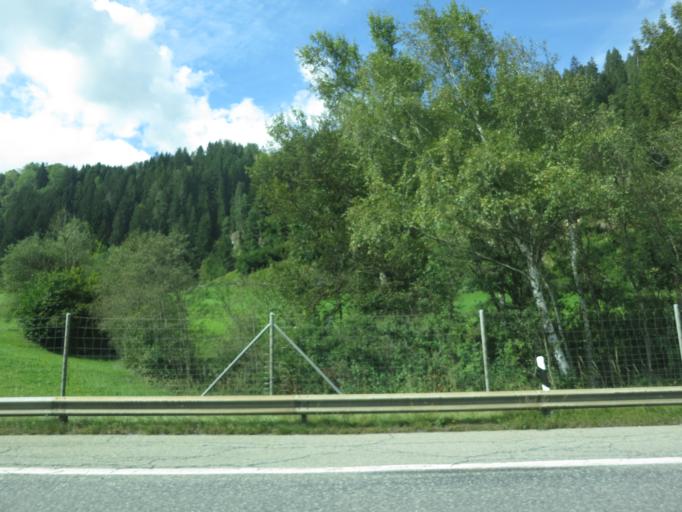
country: CH
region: Grisons
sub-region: Hinterrhein District
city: Thusis
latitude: 46.6404
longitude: 9.4411
